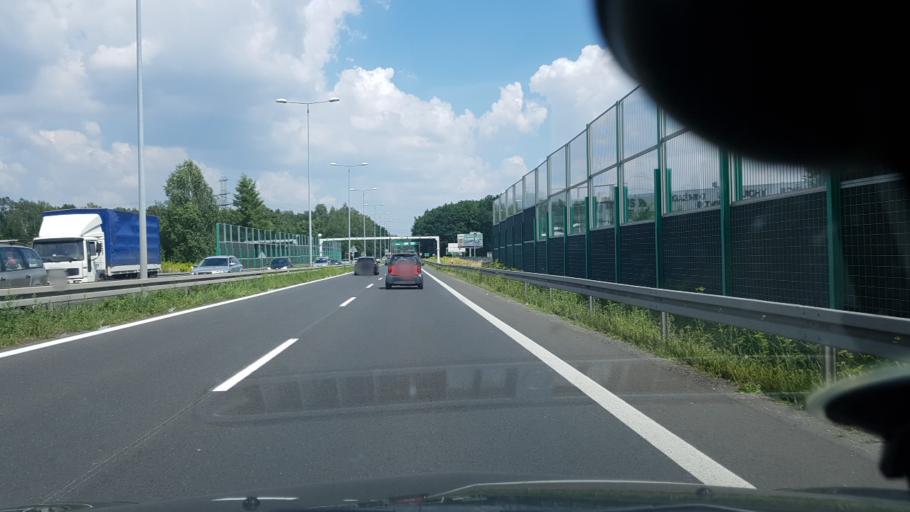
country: PL
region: Silesian Voivodeship
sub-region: Powiat mikolowski
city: Mikolow
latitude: 50.1930
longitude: 18.9267
